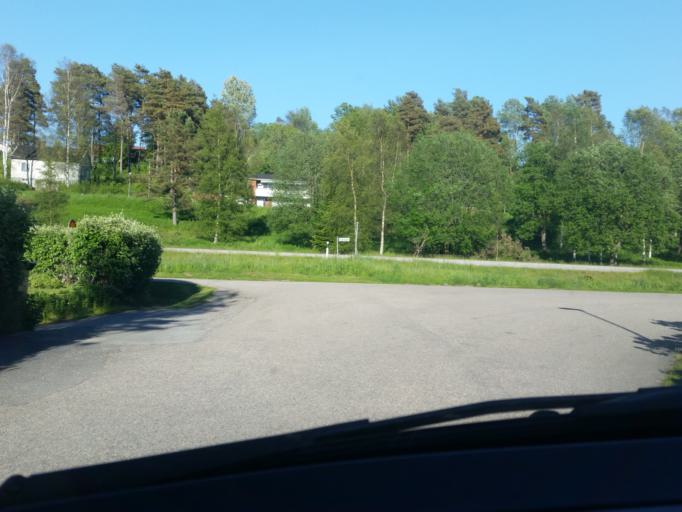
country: SE
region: Vaestra Goetaland
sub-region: Fargelanda Kommun
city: Faergelanda
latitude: 58.5690
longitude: 12.0038
